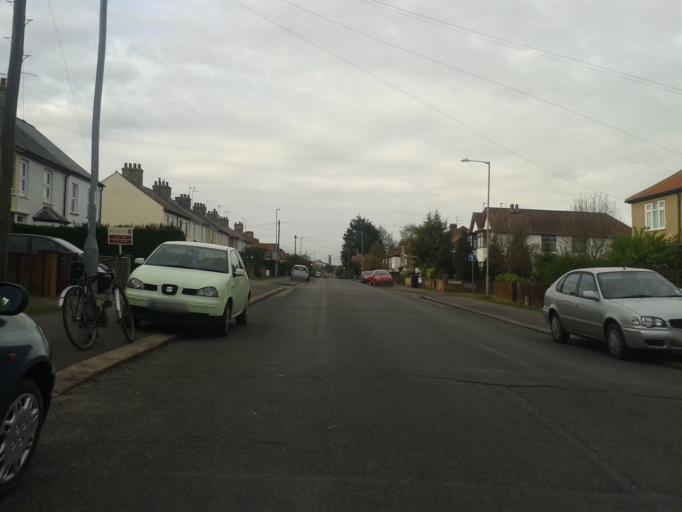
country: GB
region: England
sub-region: Cambridgeshire
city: Cambridge
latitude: 52.1946
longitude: 0.1474
